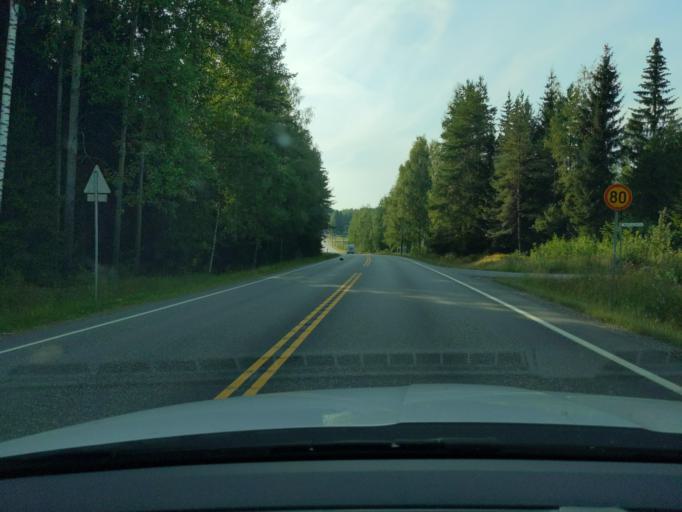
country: FI
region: Paijanne Tavastia
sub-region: Lahti
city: Padasjoki
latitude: 61.3416
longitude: 25.2546
